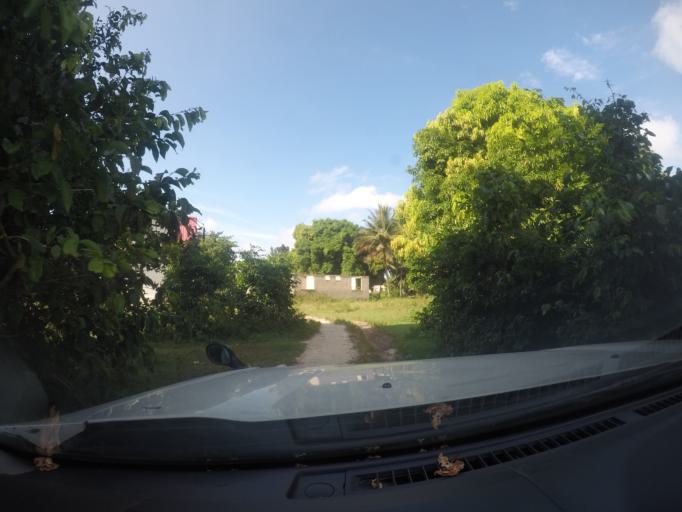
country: TZ
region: Pemba South
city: Chake Chake
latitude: -5.2488
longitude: 39.7859
